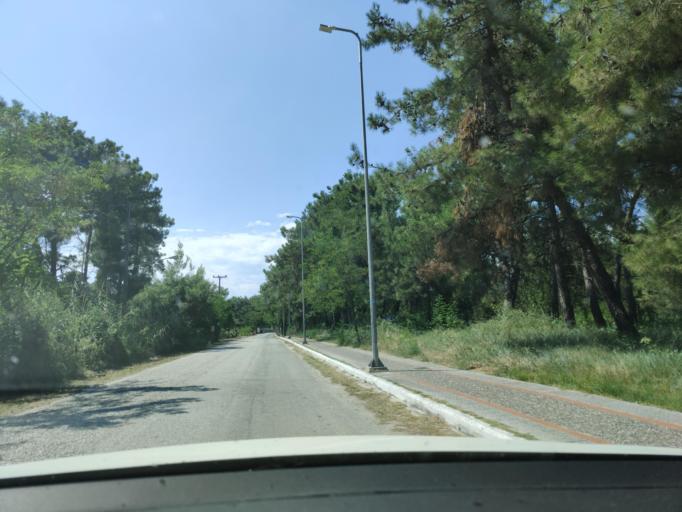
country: GR
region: East Macedonia and Thrace
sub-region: Nomos Kavalas
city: Prinos
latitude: 40.7601
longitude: 24.5678
